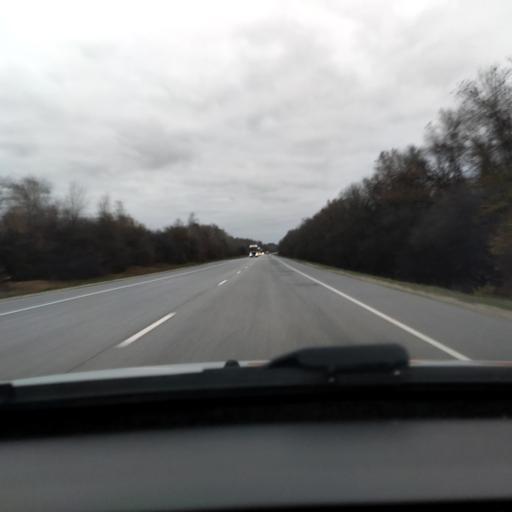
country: RU
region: Lipetsk
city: Borinskoye
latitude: 52.3650
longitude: 39.2042
